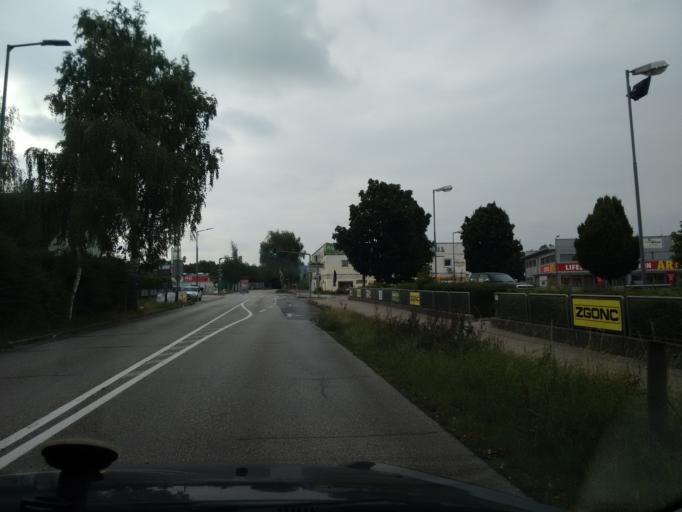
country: AT
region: Upper Austria
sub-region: Wels Stadt
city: Wels
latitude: 48.1817
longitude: 14.0172
